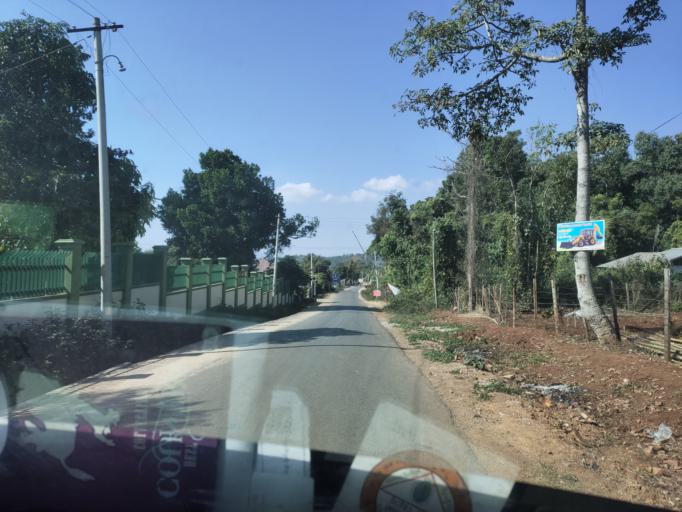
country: MM
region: Mandalay
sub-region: Pyin Oo Lwin District
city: Pyin Oo Lwin
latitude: 21.9520
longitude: 96.3969
